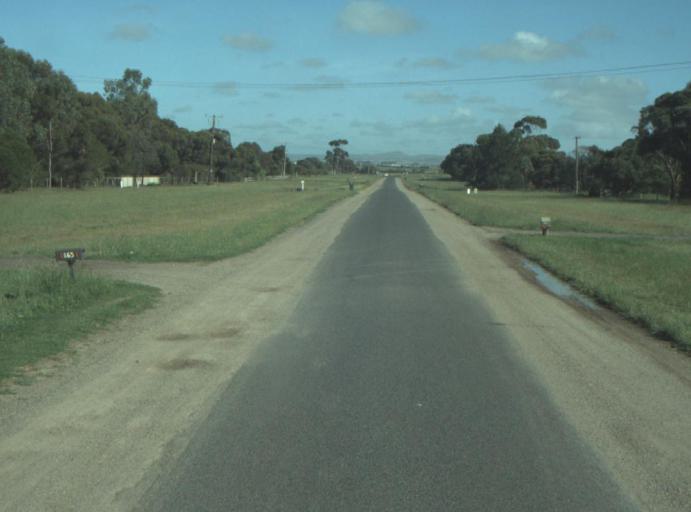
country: AU
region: Victoria
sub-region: Greater Geelong
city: Lara
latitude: -38.0103
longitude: 144.3843
